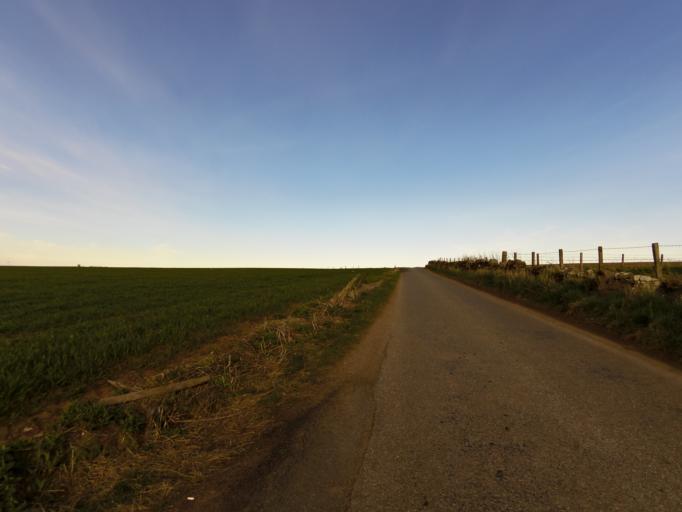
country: GB
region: Scotland
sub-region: Aberdeenshire
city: Stonehaven
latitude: 56.9112
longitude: -2.2165
